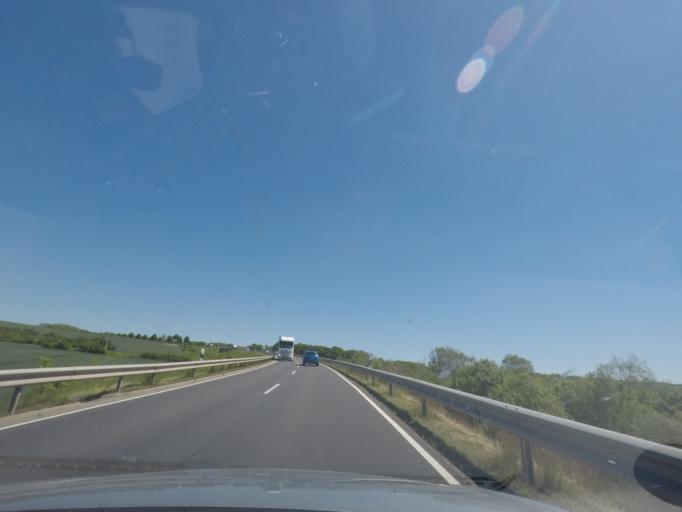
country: DE
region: Saxony-Anhalt
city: Harbke
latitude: 52.2127
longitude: 11.0337
